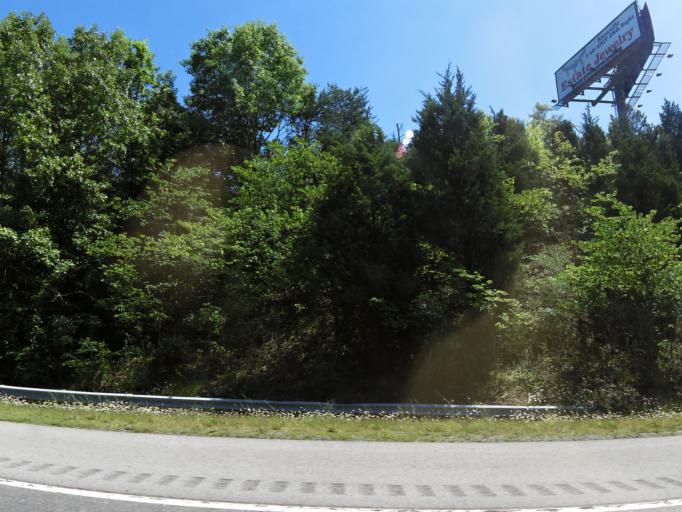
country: US
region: Tennessee
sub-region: Knox County
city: Mascot
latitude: 35.9962
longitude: -83.6893
